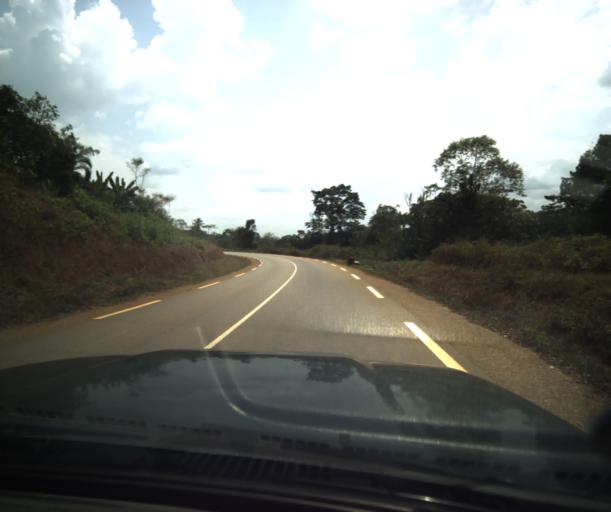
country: CM
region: Centre
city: Mbankomo
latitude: 3.6657
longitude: 11.3429
